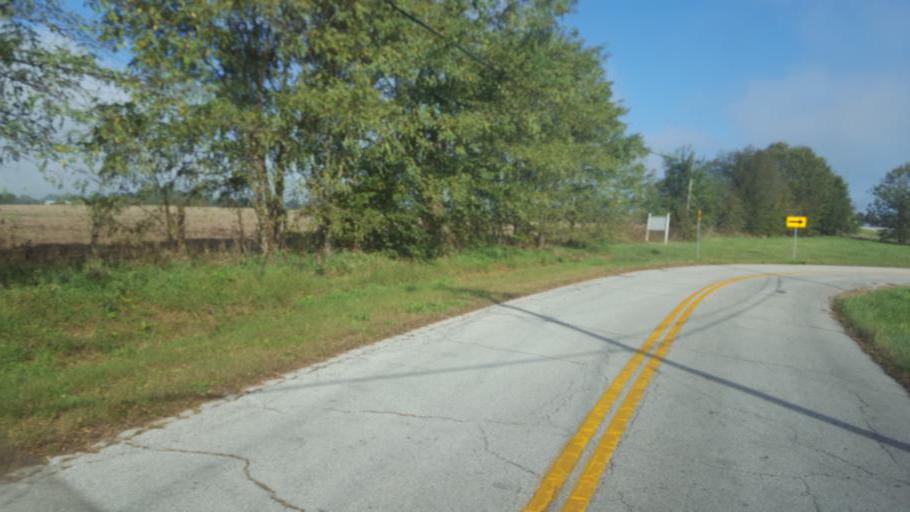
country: US
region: Kentucky
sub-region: Mason County
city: Maysville
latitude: 38.5746
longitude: -83.7787
